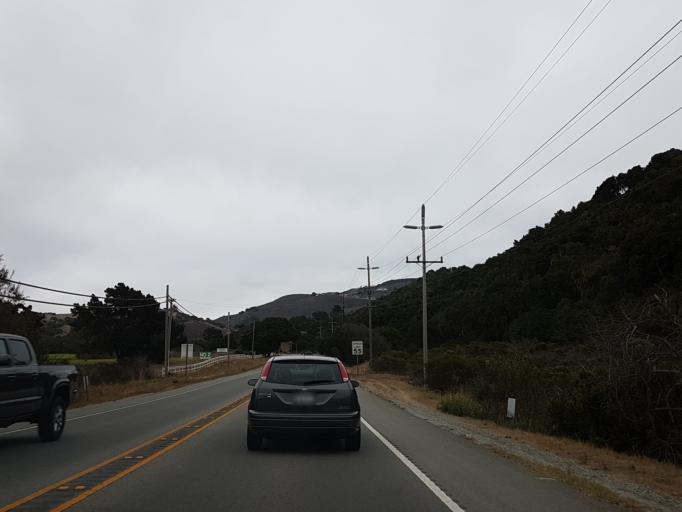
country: US
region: California
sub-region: Monterey County
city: Del Rey Oaks
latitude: 36.5694
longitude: -121.7863
